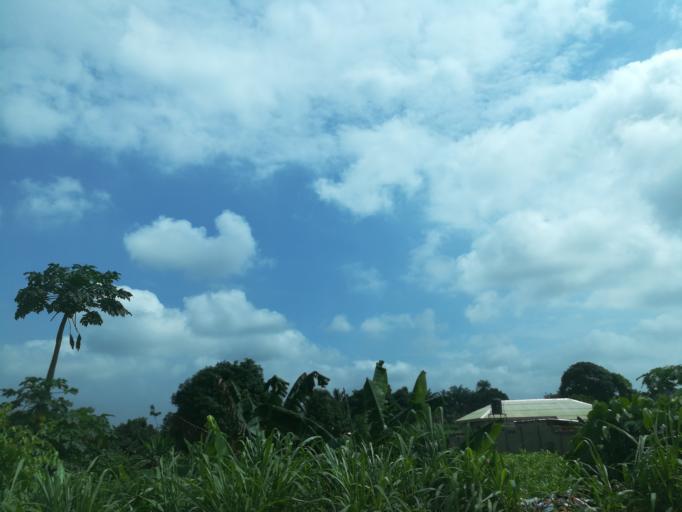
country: NG
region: Ogun
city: Odogbolu
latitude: 6.6511
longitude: 3.7058
